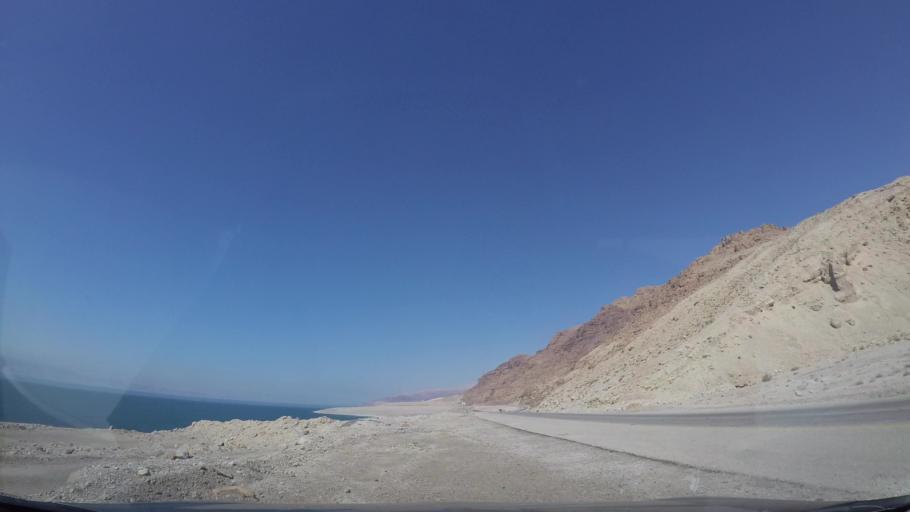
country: JO
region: Karak
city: Al Qasr
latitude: 31.3691
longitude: 35.5469
